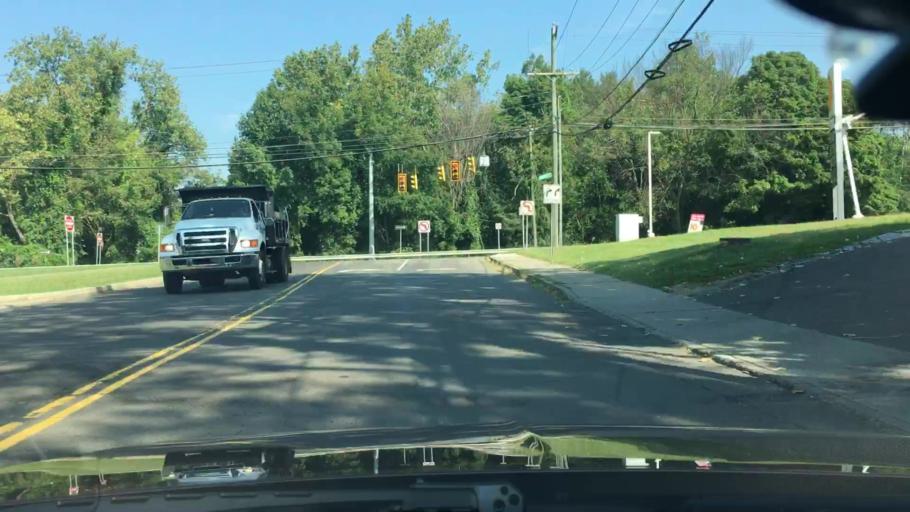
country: US
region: Connecticut
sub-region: Fairfield County
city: Bethel
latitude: 41.4126
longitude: -73.4087
